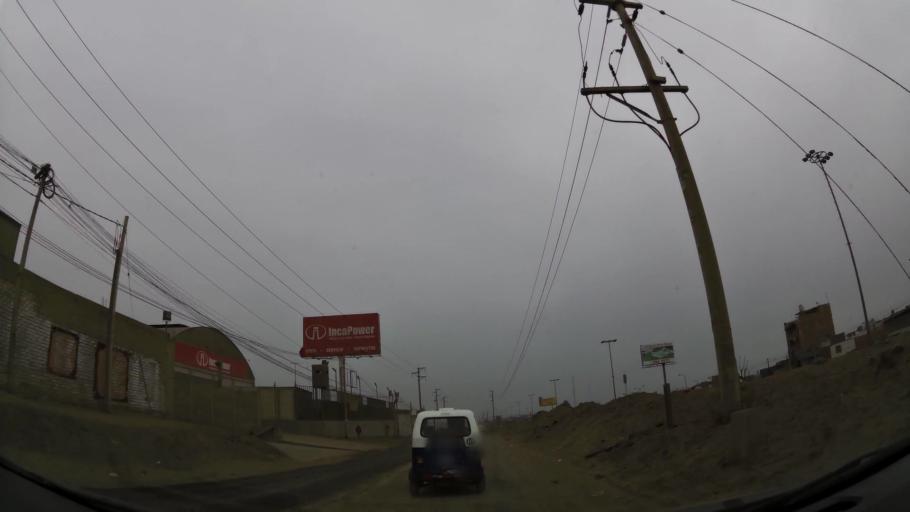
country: PE
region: Lima
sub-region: Lima
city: Surco
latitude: -12.2129
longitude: -76.9759
